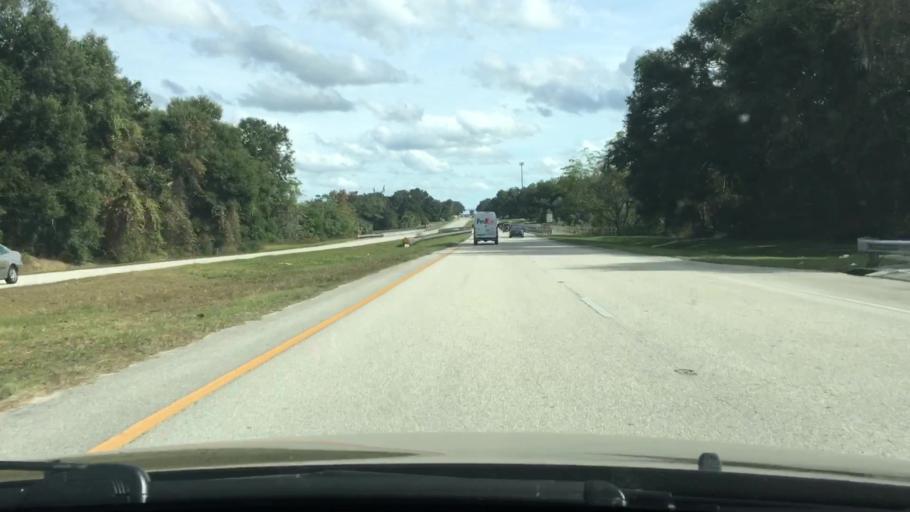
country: US
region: Florida
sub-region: Volusia County
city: North DeLand
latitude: 29.0546
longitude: -81.3137
